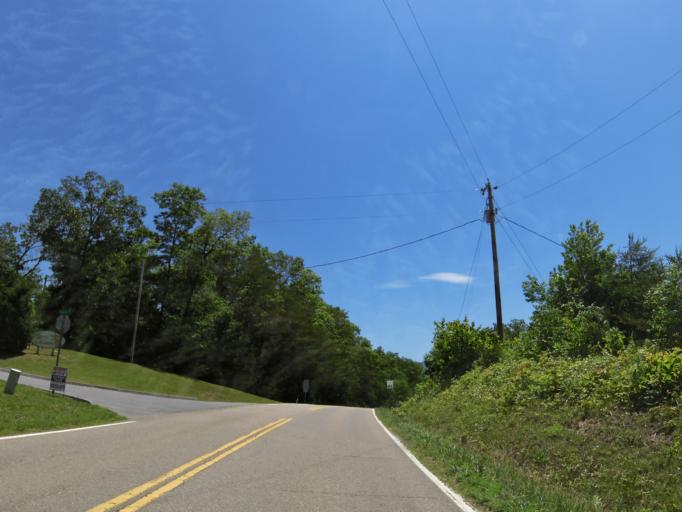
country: US
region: Tennessee
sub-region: Jefferson County
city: Dandridge
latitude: 35.9600
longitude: -83.3712
